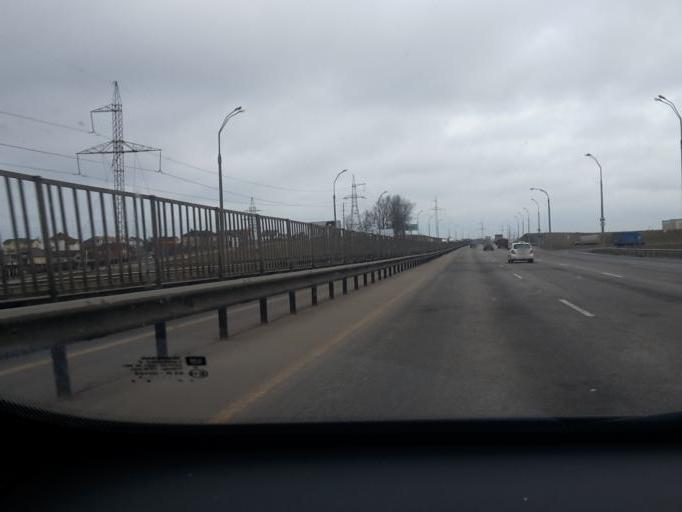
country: BY
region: Minsk
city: Zhdanovichy
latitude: 53.9164
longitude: 27.4121
